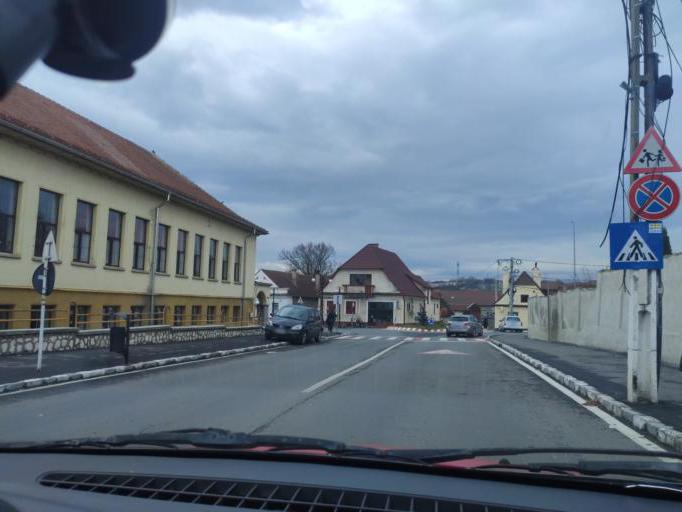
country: RO
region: Brasov
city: Codlea
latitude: 45.7005
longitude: 25.4450
